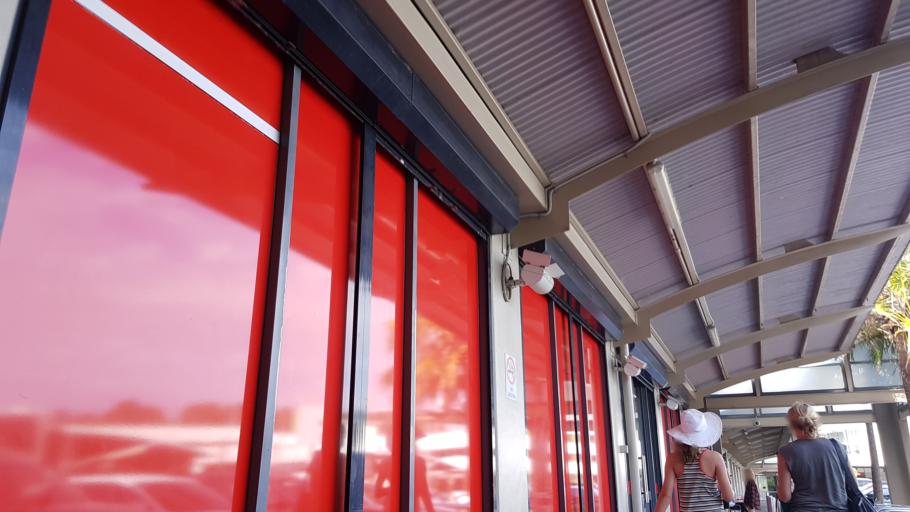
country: AU
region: New South Wales
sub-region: Pittwater
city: Warriewood
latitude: -33.6968
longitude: 151.2955
